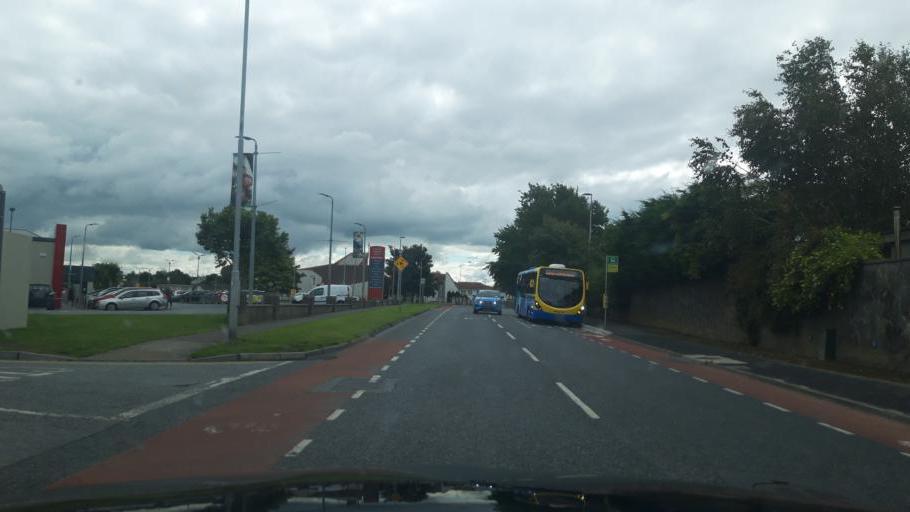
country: IE
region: Leinster
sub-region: Kilkenny
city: Kilkenny
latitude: 52.6409
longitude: -7.2439
